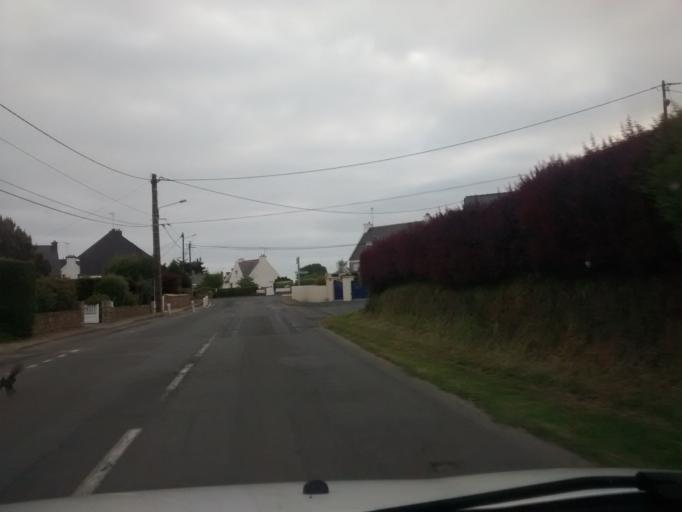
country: FR
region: Brittany
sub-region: Departement des Cotes-d'Armor
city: Tregastel
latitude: 48.8138
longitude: -3.4737
